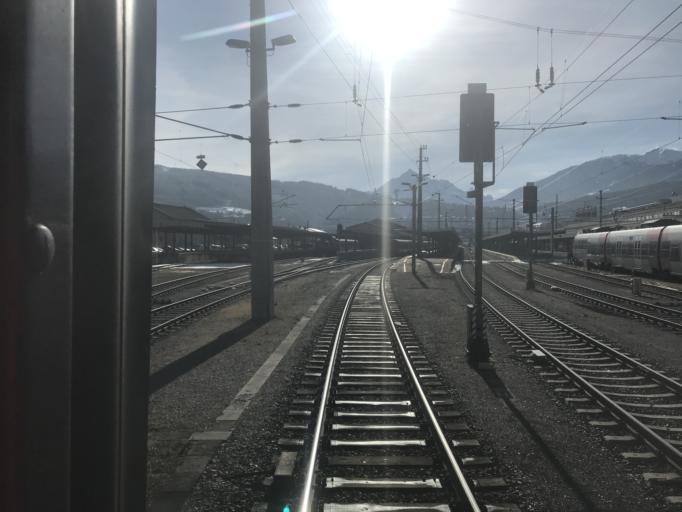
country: AT
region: Tyrol
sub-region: Innsbruck Stadt
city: Innsbruck
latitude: 47.2636
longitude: 11.4017
